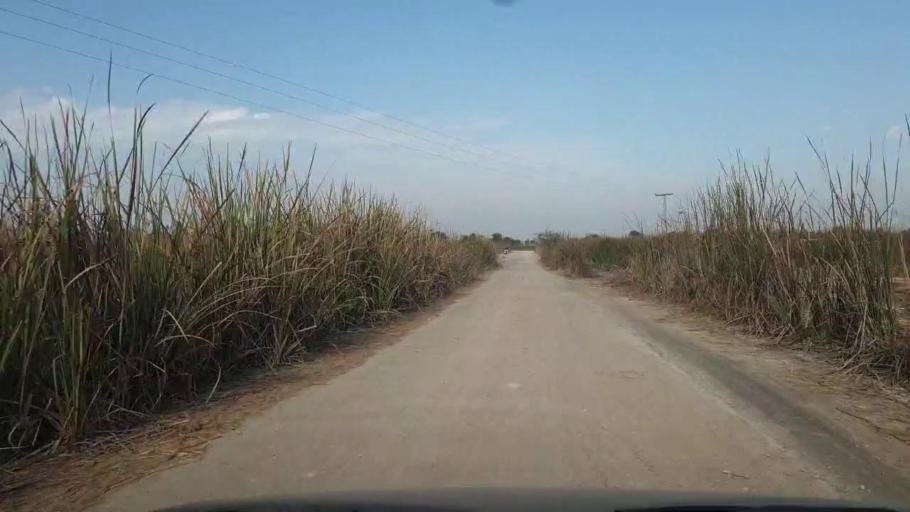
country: PK
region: Sindh
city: Sakrand
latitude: 26.0264
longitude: 68.4420
